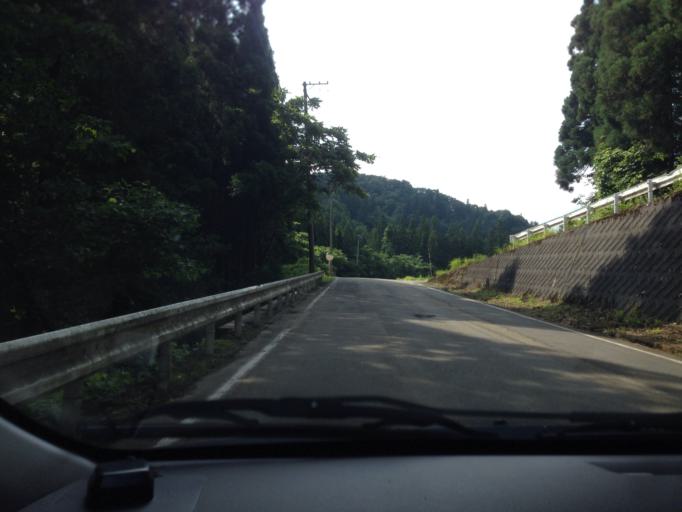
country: JP
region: Fukushima
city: Kitakata
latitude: 37.4251
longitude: 139.5401
